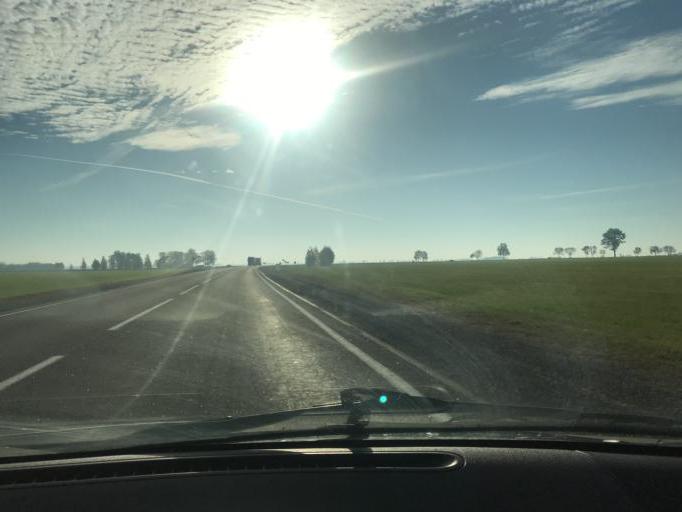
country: BY
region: Brest
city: Drahichyn
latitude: 52.2066
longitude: 25.2227
